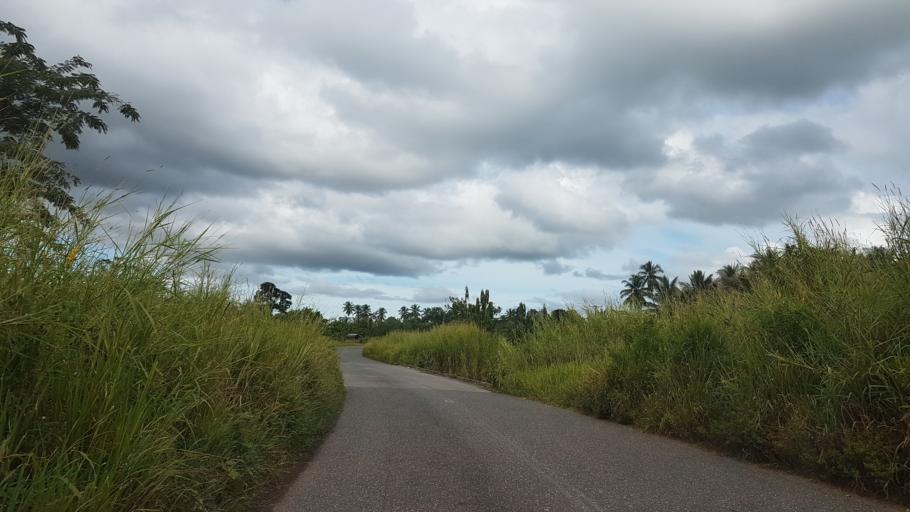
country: PG
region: Northern Province
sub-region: Sohe
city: Popondetta
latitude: -8.8025
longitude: 148.2303
